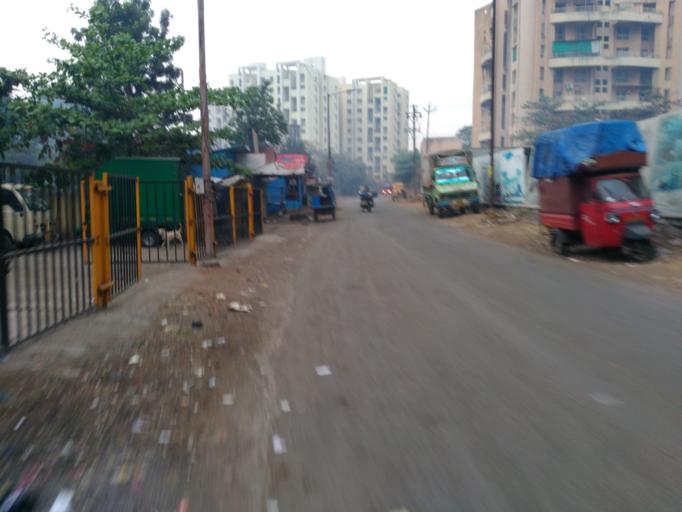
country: IN
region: Maharashtra
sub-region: Pune Division
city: Pune
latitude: 18.4607
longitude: 73.8884
